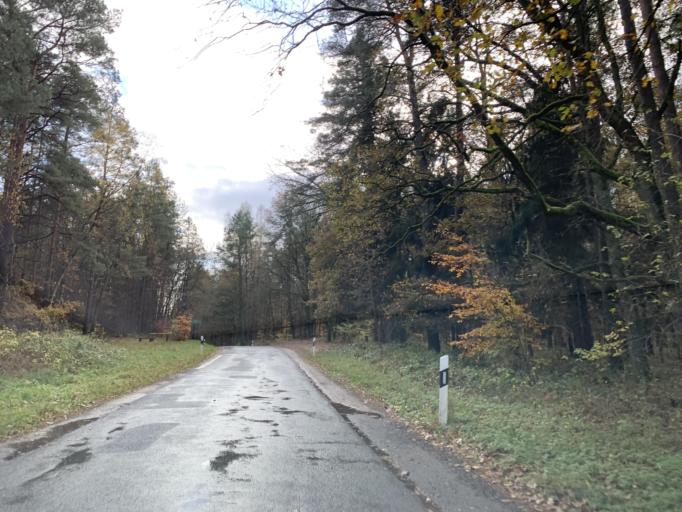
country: DE
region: Mecklenburg-Vorpommern
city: Blankensee
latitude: 53.3947
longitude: 13.2617
